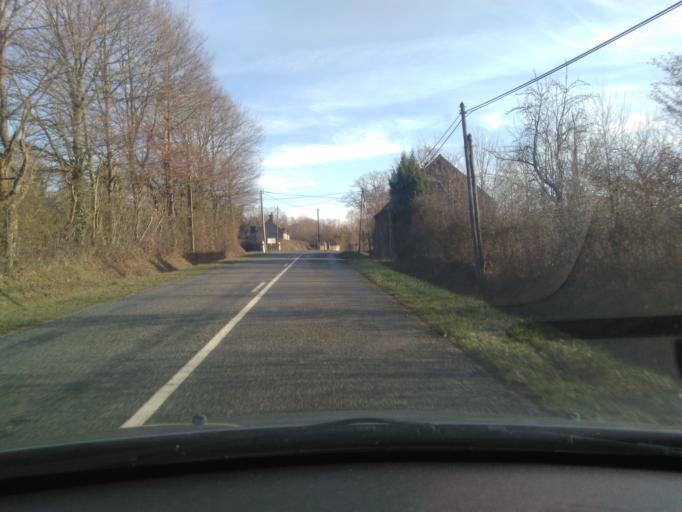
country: FR
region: Centre
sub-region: Departement du Cher
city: Chateaumeillant
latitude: 46.6337
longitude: 2.1661
